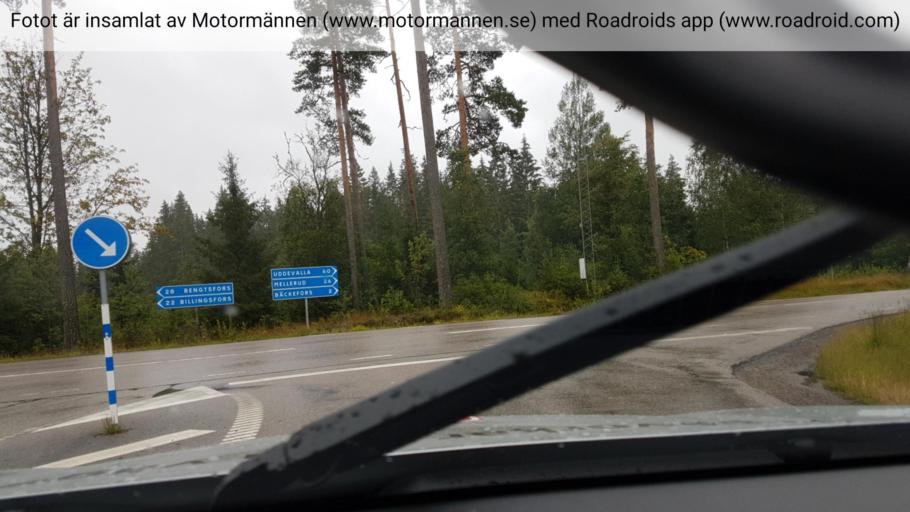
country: SE
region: Vaestra Goetaland
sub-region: Bengtsfors Kommun
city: Dals Langed
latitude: 58.8258
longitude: 12.1391
